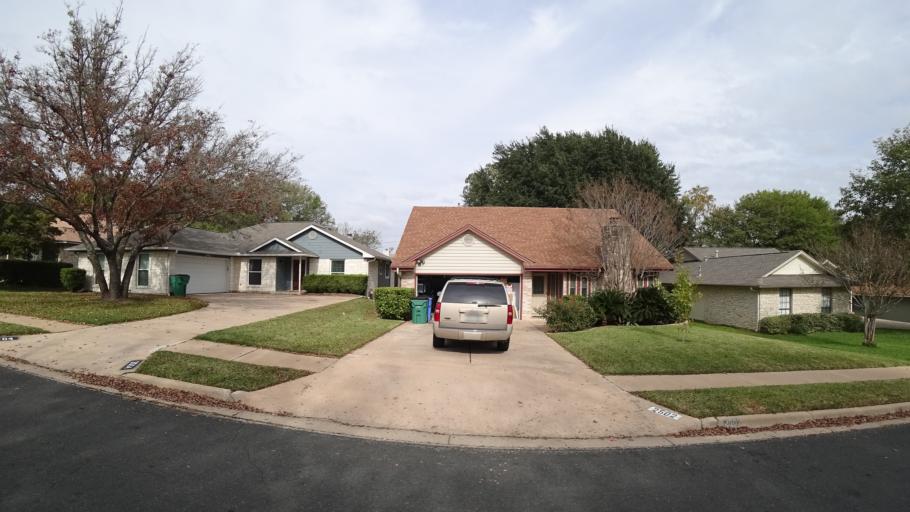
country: US
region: Texas
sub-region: Travis County
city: Wells Branch
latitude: 30.4462
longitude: -97.6841
